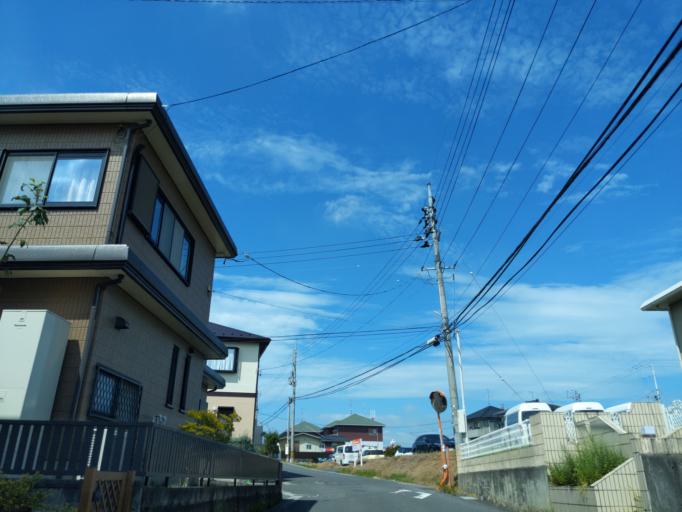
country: JP
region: Fukushima
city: Koriyama
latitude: 37.4210
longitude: 140.3836
